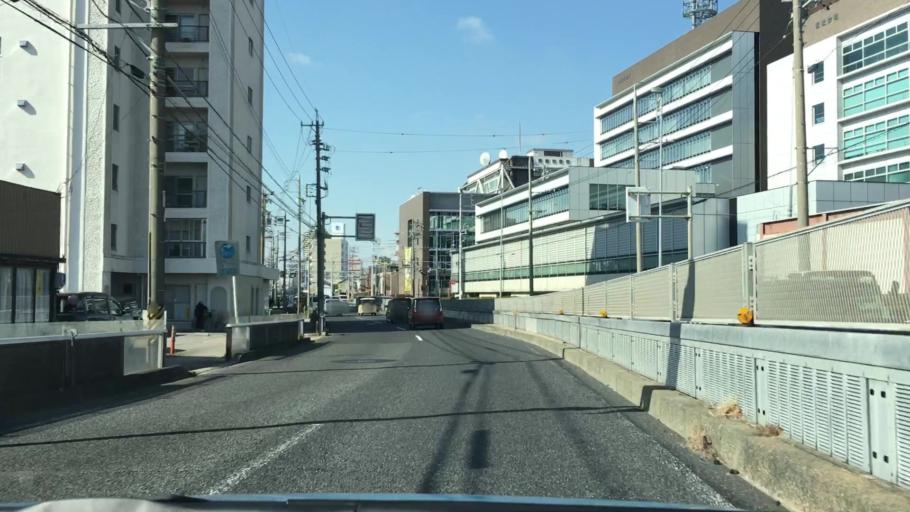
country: JP
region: Aichi
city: Okazaki
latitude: 34.9537
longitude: 137.1752
